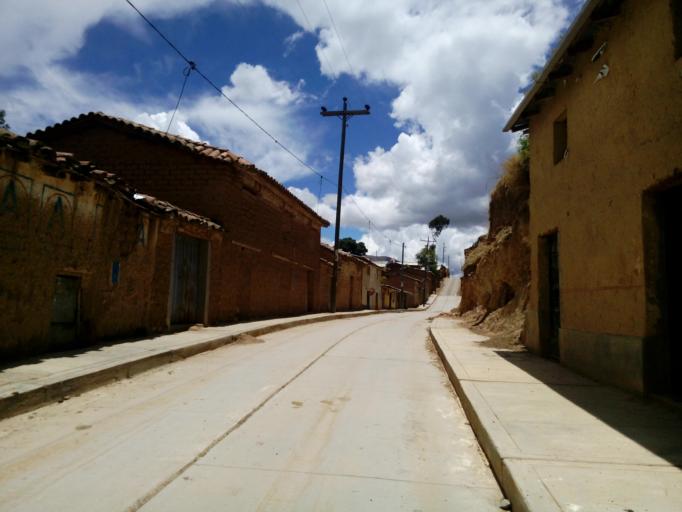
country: PE
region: Ayacucho
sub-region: Provincia de Victor Fajardo
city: Canaria
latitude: -13.8779
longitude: -73.9345
